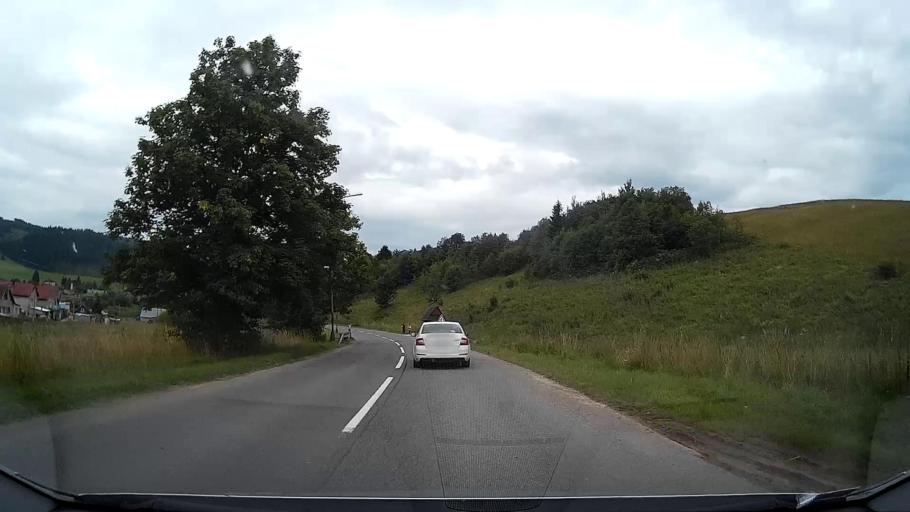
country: SK
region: Banskobystricky
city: Revuca
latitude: 48.8447
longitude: 20.1822
